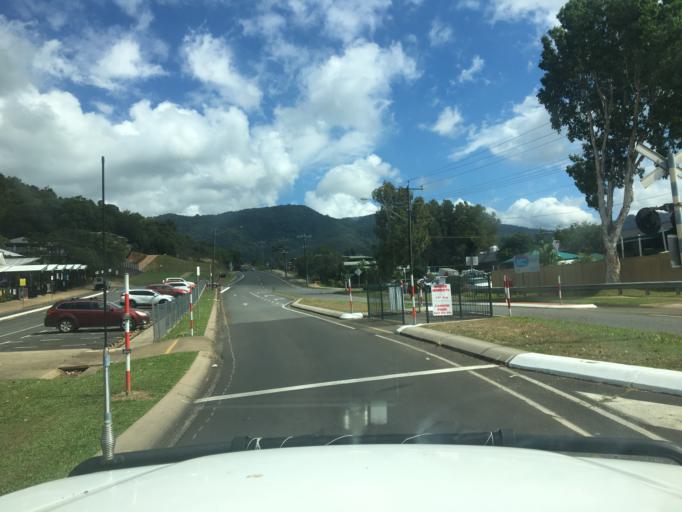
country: AU
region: Queensland
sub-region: Cairns
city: Woree
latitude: -16.9674
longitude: 145.7411
